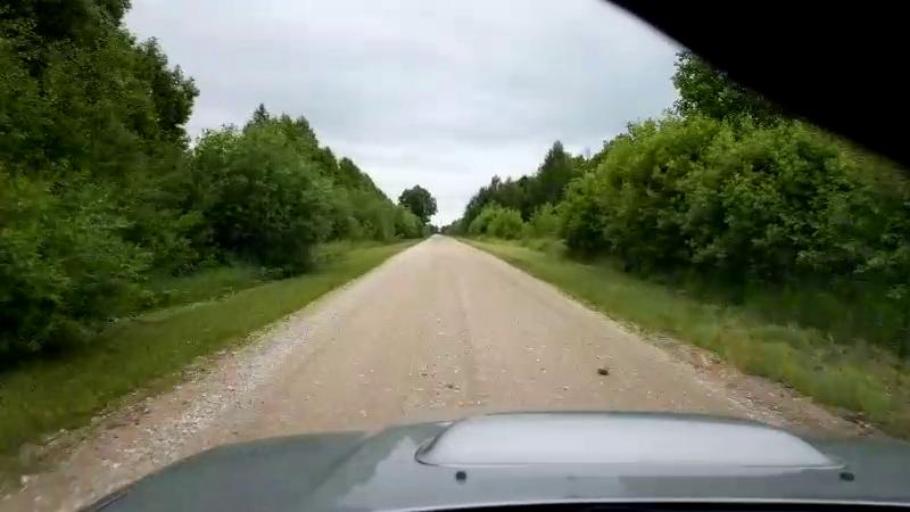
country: EE
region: Paernumaa
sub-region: Halinga vald
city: Parnu-Jaagupi
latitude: 58.5473
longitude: 24.5602
